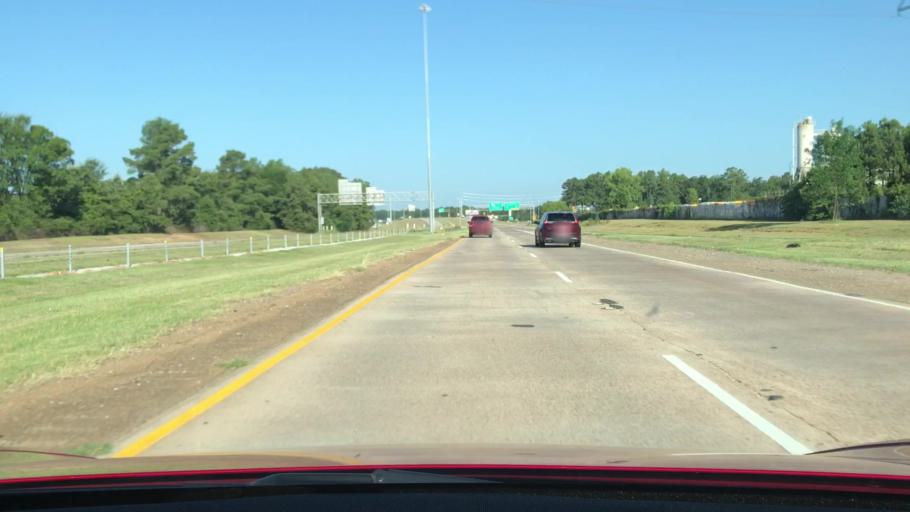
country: US
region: Louisiana
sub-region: Bossier Parish
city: Bossier City
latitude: 32.4199
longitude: -93.7548
